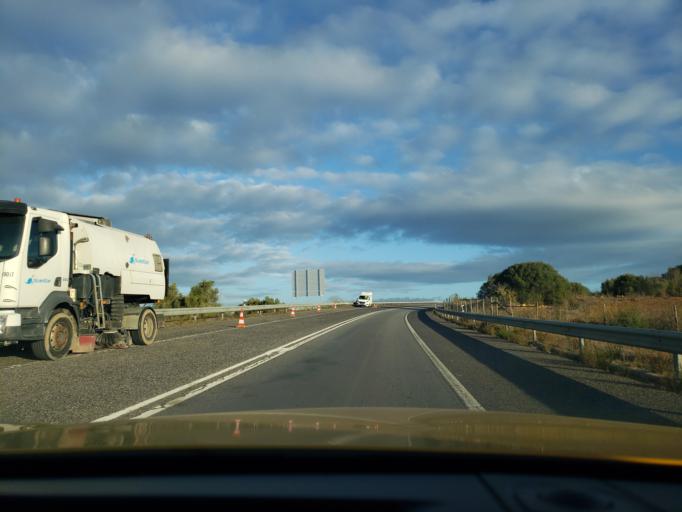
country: PT
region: Faro
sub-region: Portimao
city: Alvor
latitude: 37.1649
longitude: -8.5698
